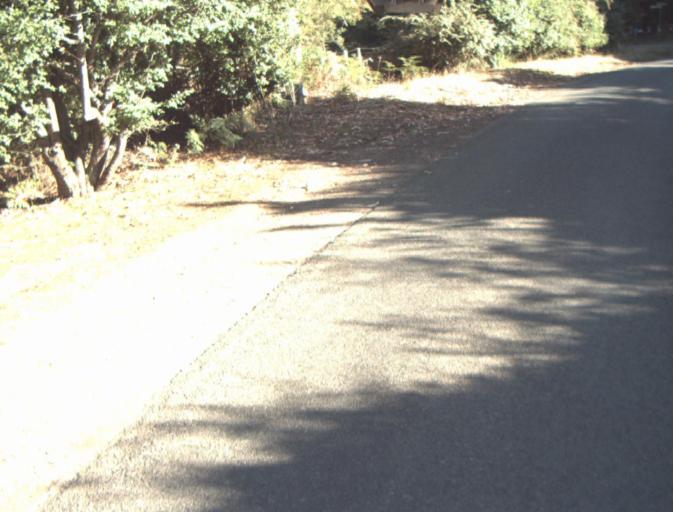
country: AU
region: Tasmania
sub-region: Launceston
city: Mayfield
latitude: -41.3039
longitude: 147.1983
